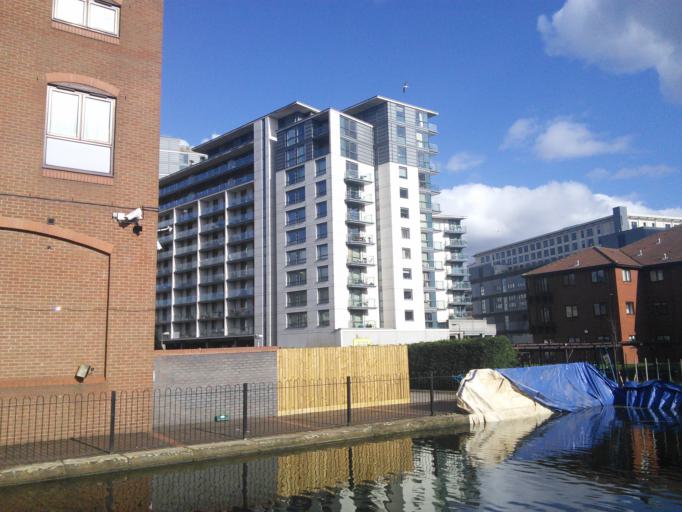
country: GB
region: England
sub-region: City and Borough of Birmingham
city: Birmingham
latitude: 52.4764
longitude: -1.9081
